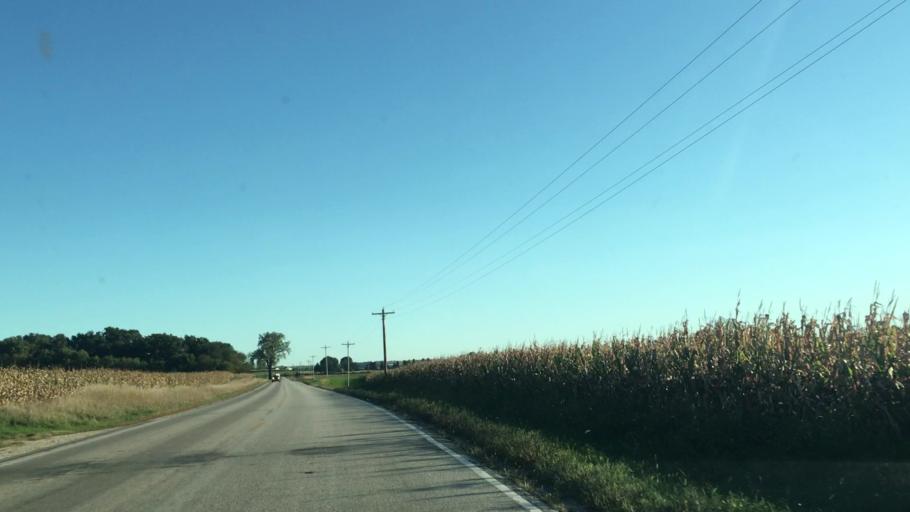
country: US
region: Minnesota
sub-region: Fillmore County
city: Chatfield
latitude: 43.8256
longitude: -92.0695
